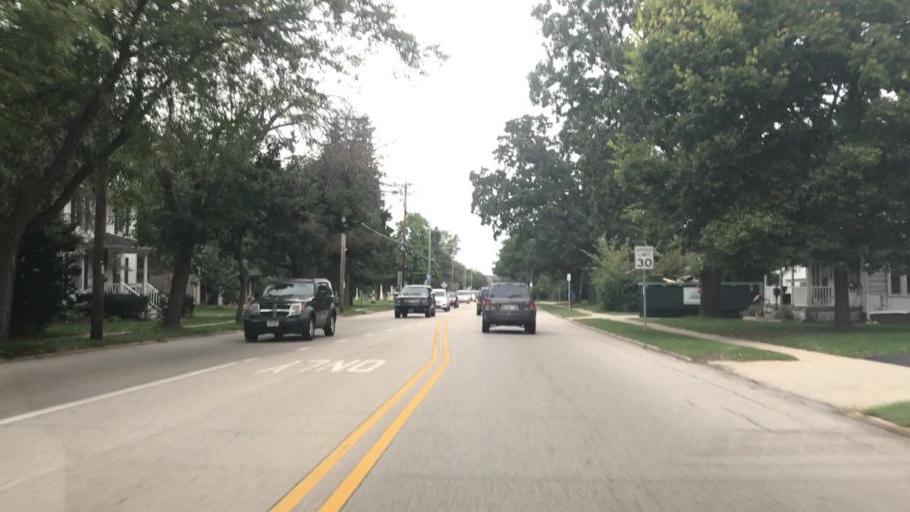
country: US
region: Wisconsin
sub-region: Waukesha County
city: Mukwonago
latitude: 42.8662
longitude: -88.3340
